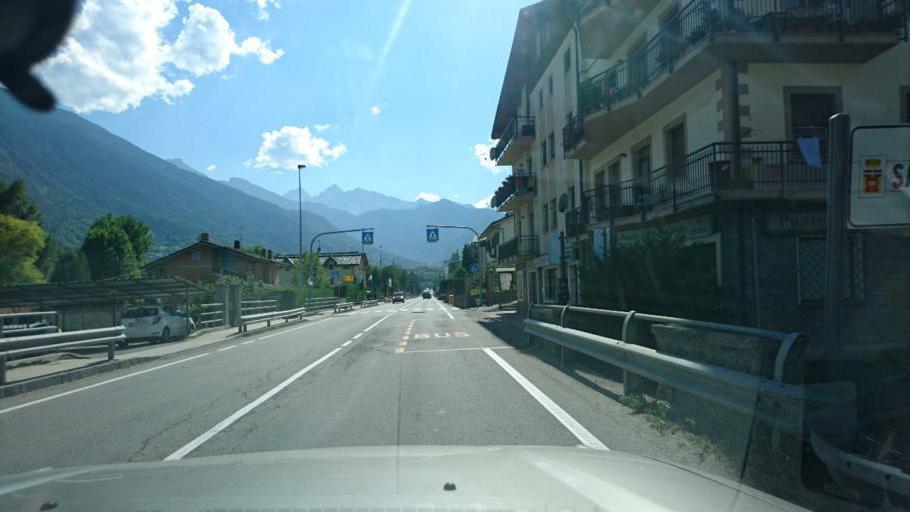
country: IT
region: Aosta Valley
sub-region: Valle d'Aosta
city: Saint Maurice
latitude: 45.7179
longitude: 7.2619
